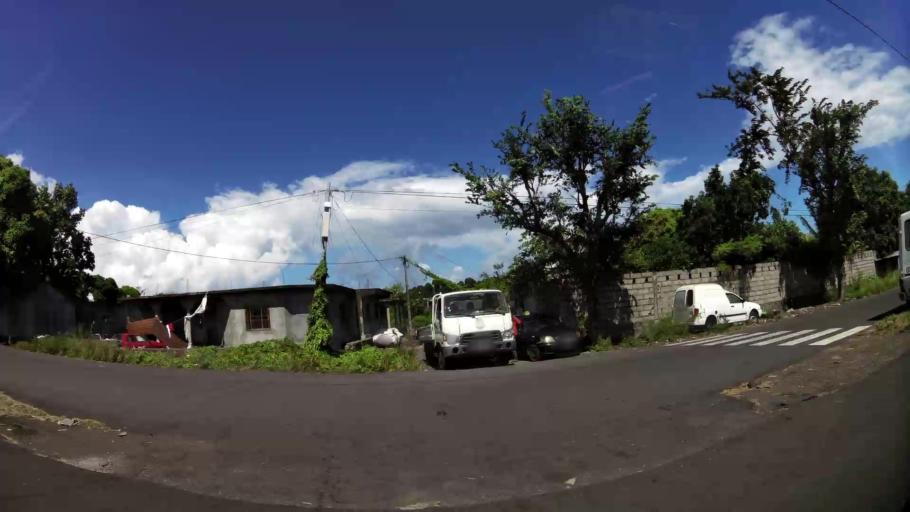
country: KM
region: Grande Comore
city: Mavingouni
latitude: -11.7190
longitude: 43.2442
